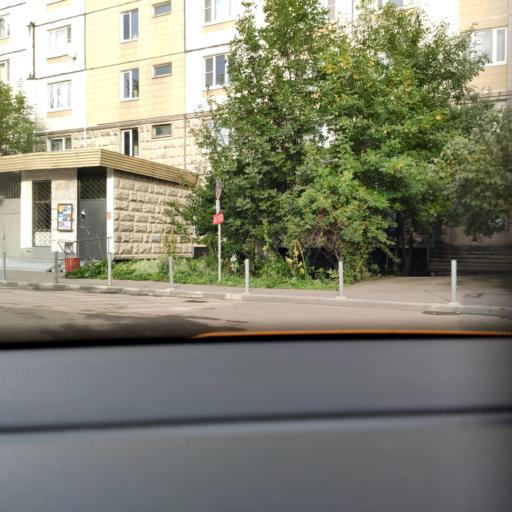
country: RU
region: Moskovskaya
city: Pavshino
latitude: 55.8432
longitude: 37.3646
